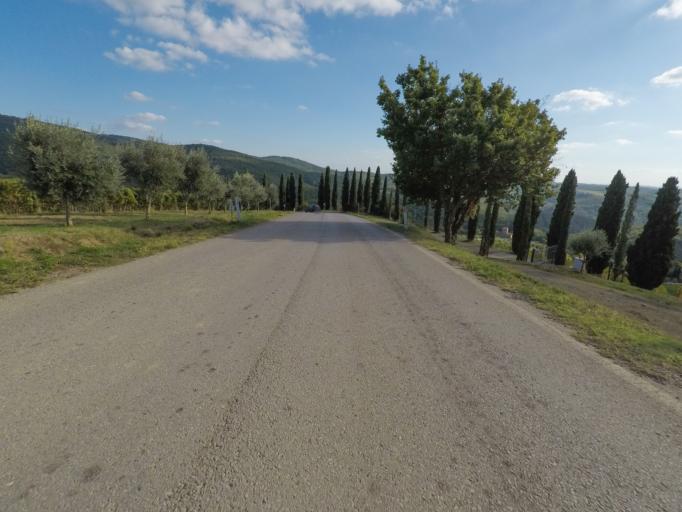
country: IT
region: Tuscany
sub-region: Provincia di Siena
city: Radda in Chianti
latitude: 43.5173
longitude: 11.4044
